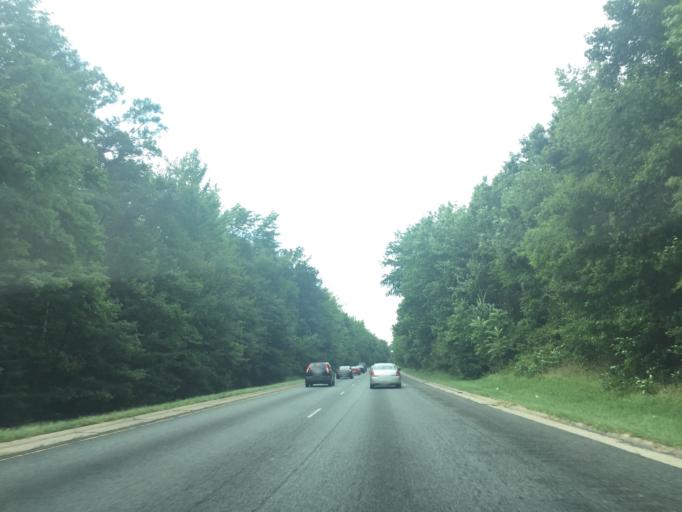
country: US
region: Maryland
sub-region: Anne Arundel County
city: Jessup
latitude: 39.1298
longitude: -76.7618
